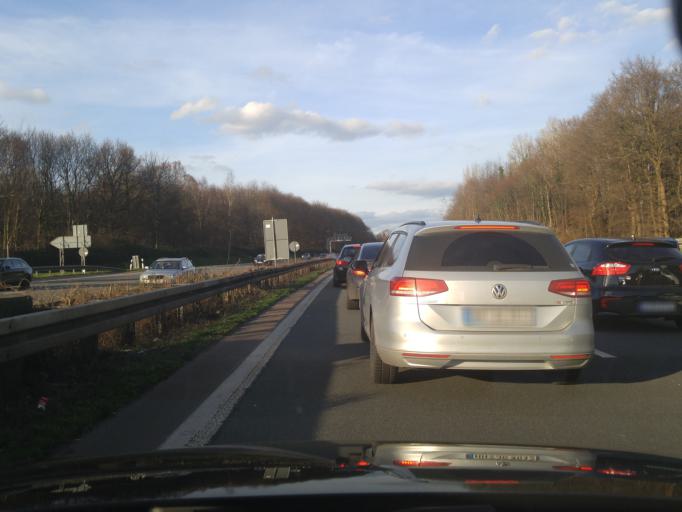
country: DE
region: North Rhine-Westphalia
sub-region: Regierungsbezirk Koln
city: Leverkusen
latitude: 51.0569
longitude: 6.9911
